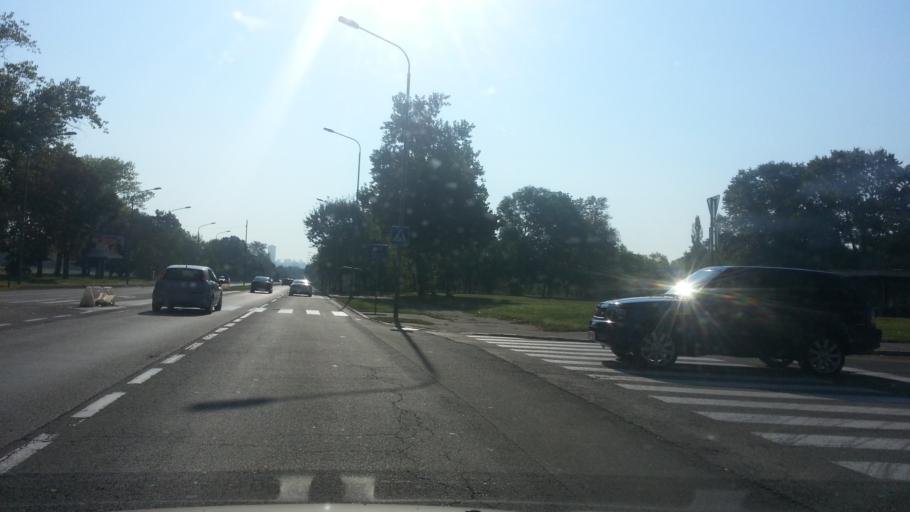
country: RS
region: Central Serbia
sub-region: Belgrade
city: Novi Beograd
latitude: 44.8207
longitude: 20.4304
